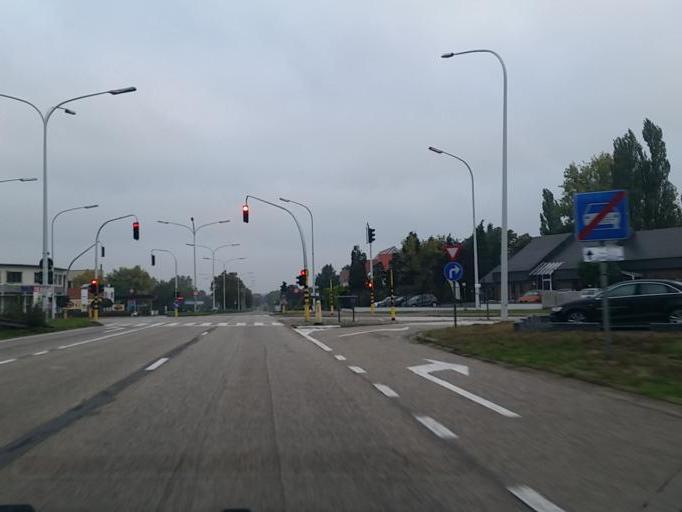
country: BE
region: Flanders
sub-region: Provincie Antwerpen
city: Kontich
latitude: 51.1370
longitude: 4.4394
